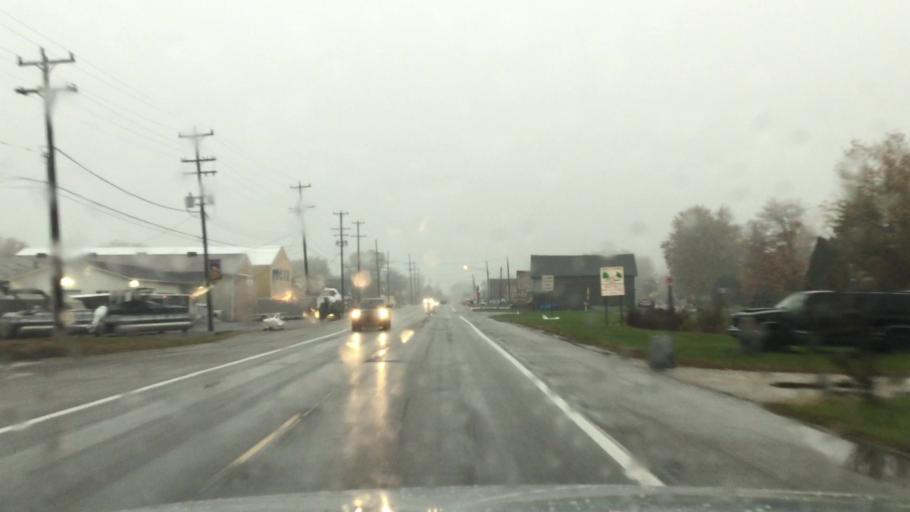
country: US
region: Michigan
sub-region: Saint Clair County
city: Pearl Beach
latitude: 42.6795
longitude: -82.6547
